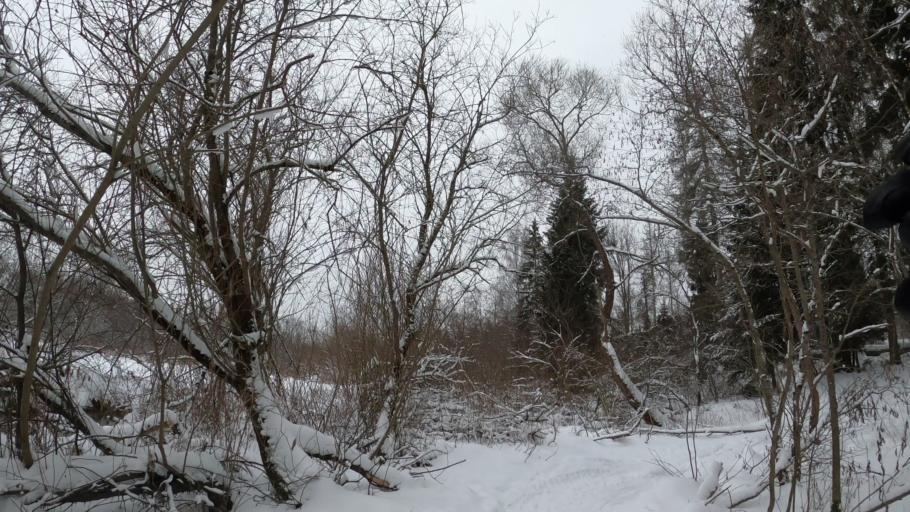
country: RU
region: Moskovskaya
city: Firsanovka
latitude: 55.9395
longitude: 37.2221
